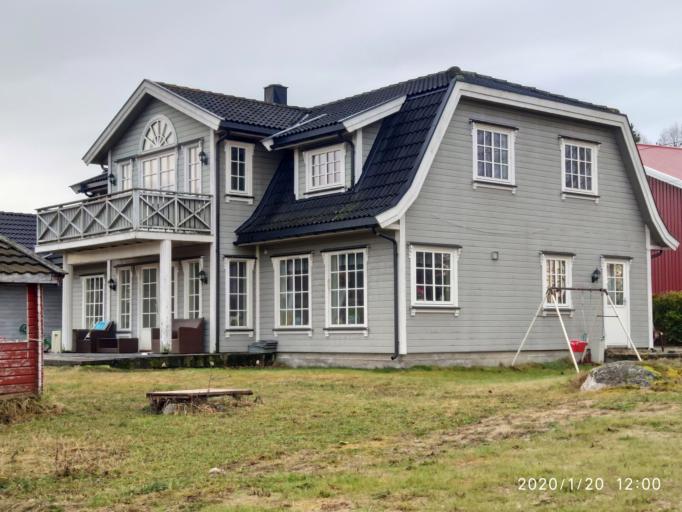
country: NO
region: Hedmark
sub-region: Grue
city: Kirkenaer
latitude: 60.4988
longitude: 12.0974
